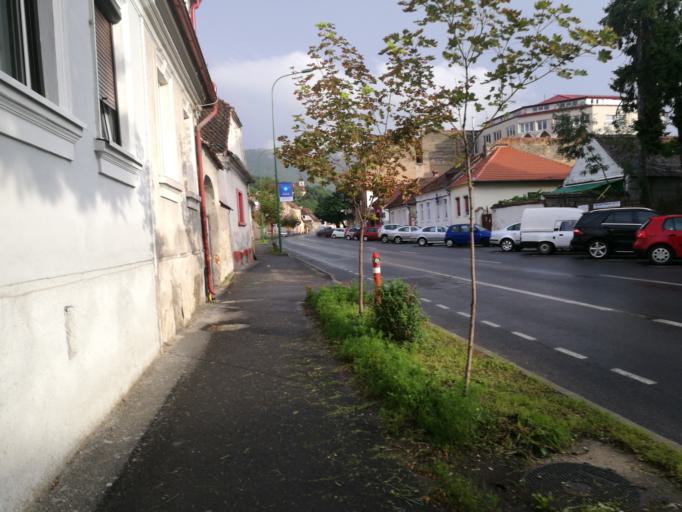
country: RO
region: Brasov
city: Brasov
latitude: 45.6552
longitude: 25.5861
